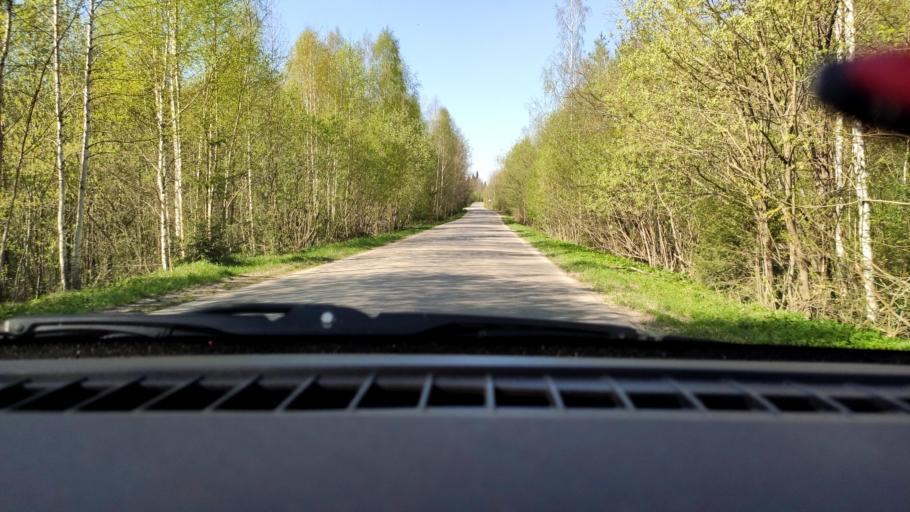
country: RU
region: Perm
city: Overyata
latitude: 58.0688
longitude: 56.0017
